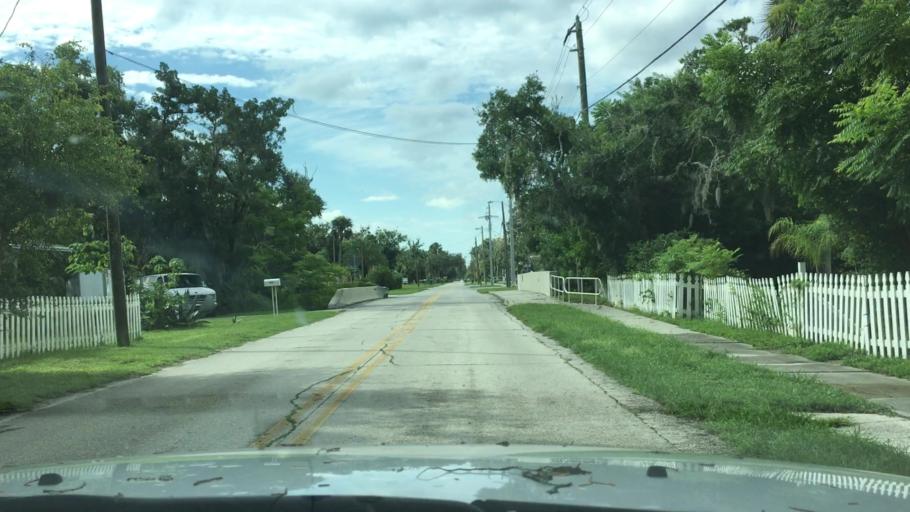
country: US
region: Florida
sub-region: Volusia County
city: Holly Hill
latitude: 29.2464
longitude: -81.0396
